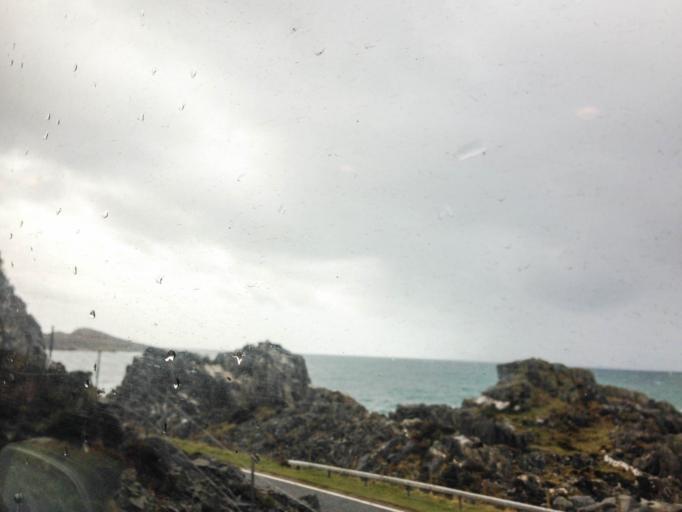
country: GB
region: Scotland
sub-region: Highland
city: Portree
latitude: 56.9998
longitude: -5.8333
